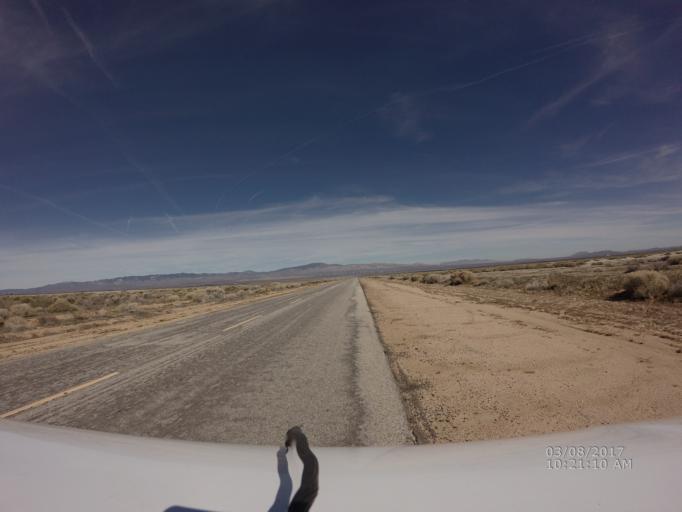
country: US
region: California
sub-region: Los Angeles County
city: Green Valley
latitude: 34.7534
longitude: -118.4312
